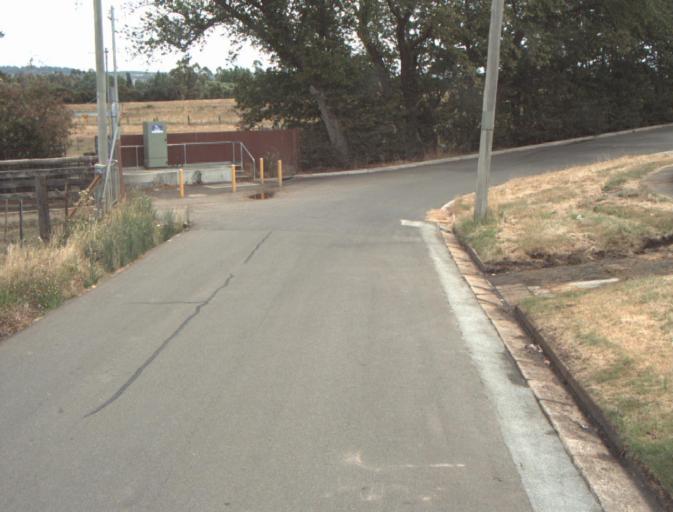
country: AU
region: Tasmania
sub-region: Launceston
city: Newnham
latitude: -41.4129
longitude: 147.1485
